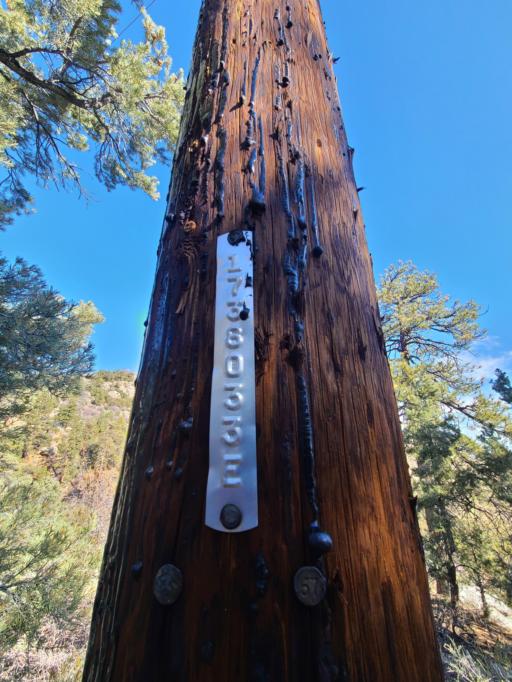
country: US
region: California
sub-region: San Bernardino County
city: Big Bear City
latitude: 34.3033
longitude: -116.8419
